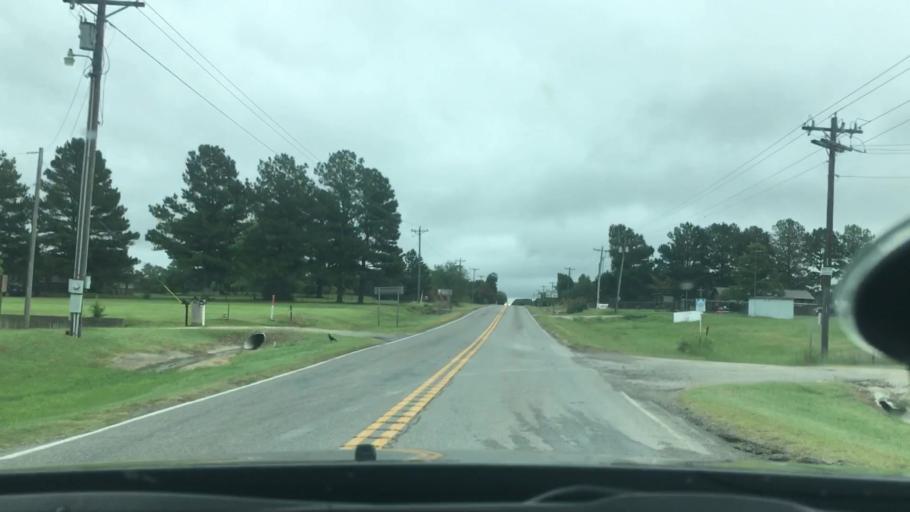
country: US
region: Oklahoma
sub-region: Sequoyah County
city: Vian
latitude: 35.6097
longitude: -94.9758
